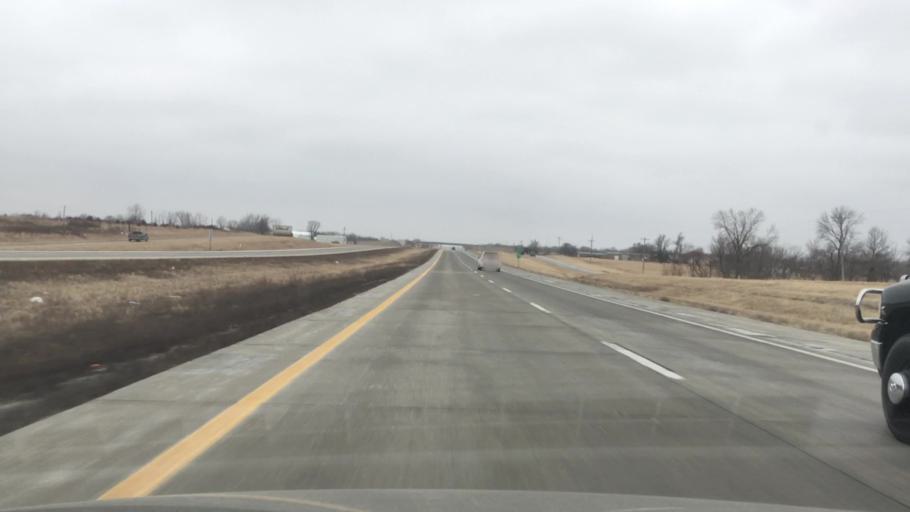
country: US
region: Missouri
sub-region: Cass County
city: Harrisonville
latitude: 38.6121
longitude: -94.3488
